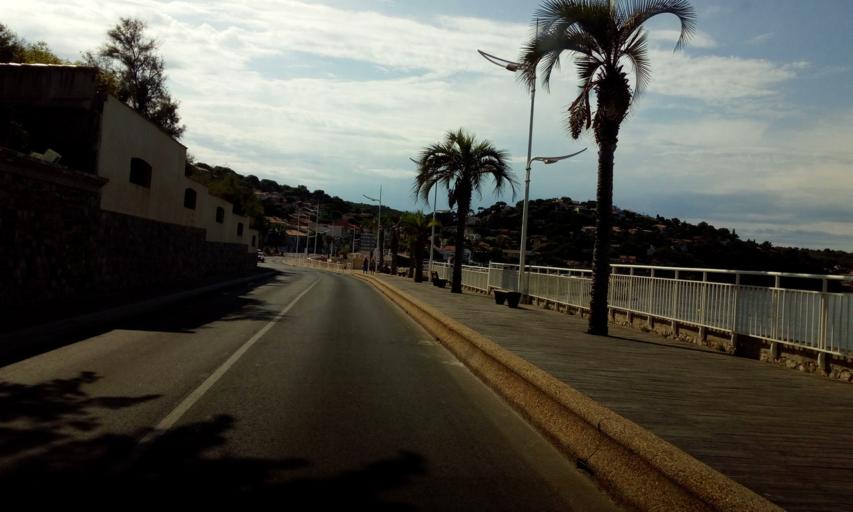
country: FR
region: Provence-Alpes-Cote d'Azur
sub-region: Departement du Var
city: Le Pradet
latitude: 43.0941
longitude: 6.0242
